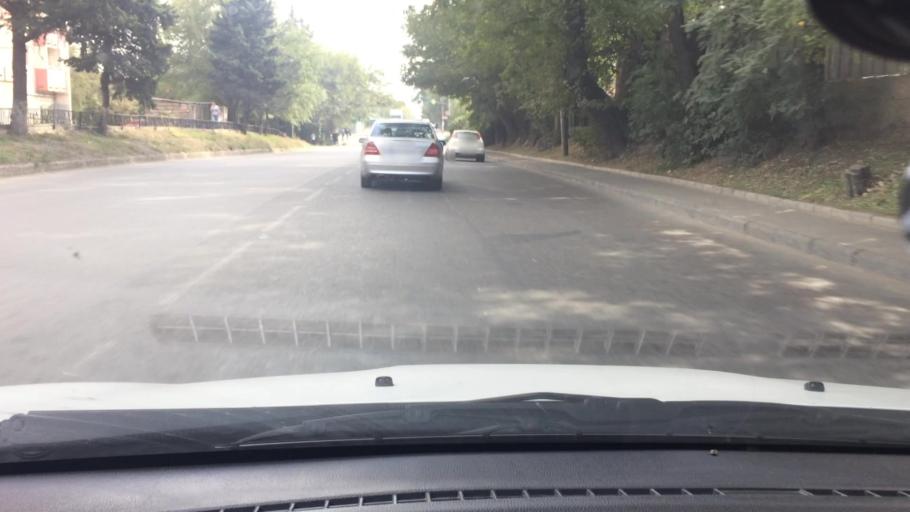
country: GE
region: T'bilisi
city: Tbilisi
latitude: 41.6490
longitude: 44.9089
